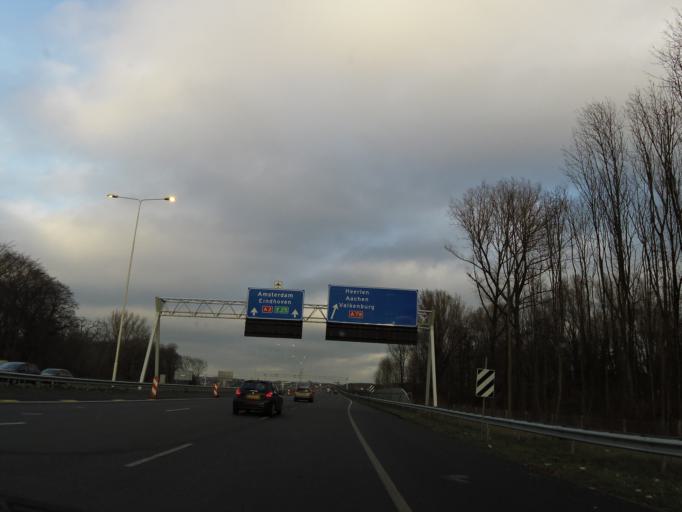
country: NL
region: Limburg
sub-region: Gemeente Maastricht
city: Heer
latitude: 50.8663
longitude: 5.7240
